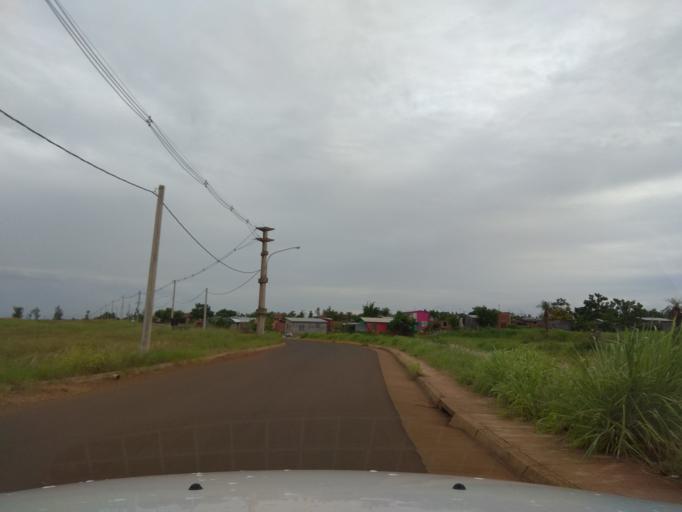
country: AR
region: Misiones
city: Garupa
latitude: -27.4290
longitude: -55.8704
